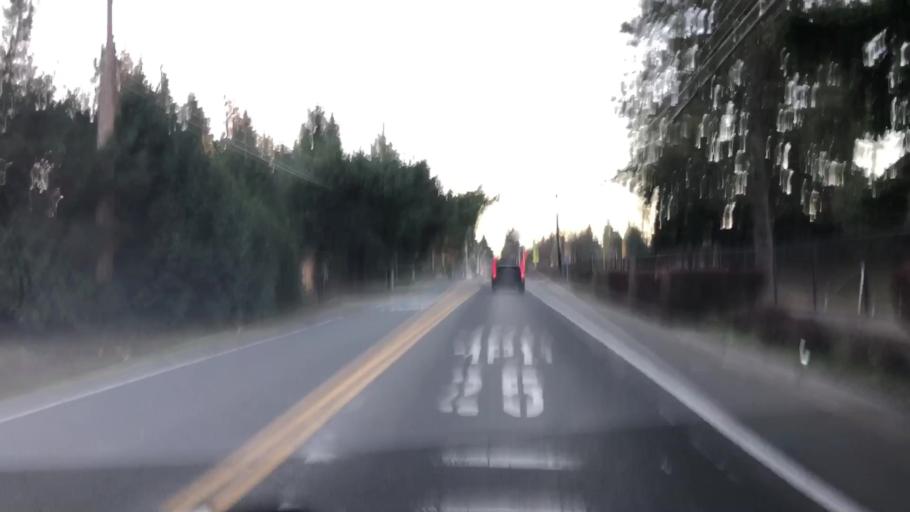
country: US
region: Washington
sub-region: King County
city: Kirkland
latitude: 47.6743
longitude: -122.1775
